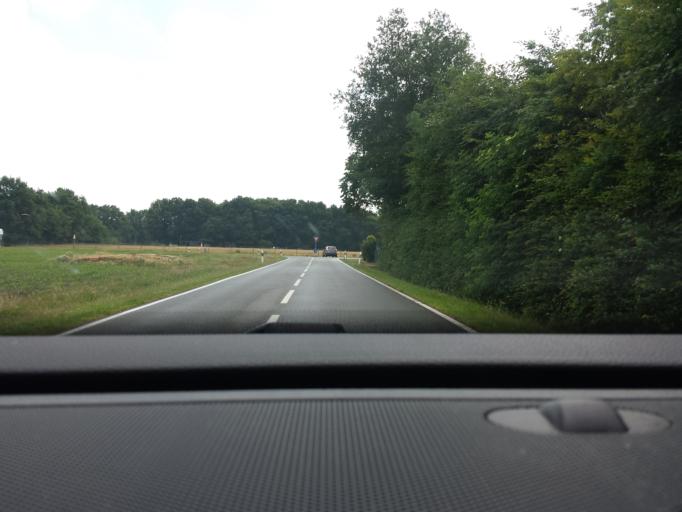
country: NL
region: Gelderland
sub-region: Berkelland
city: Eibergen
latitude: 52.0545
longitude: 6.7037
